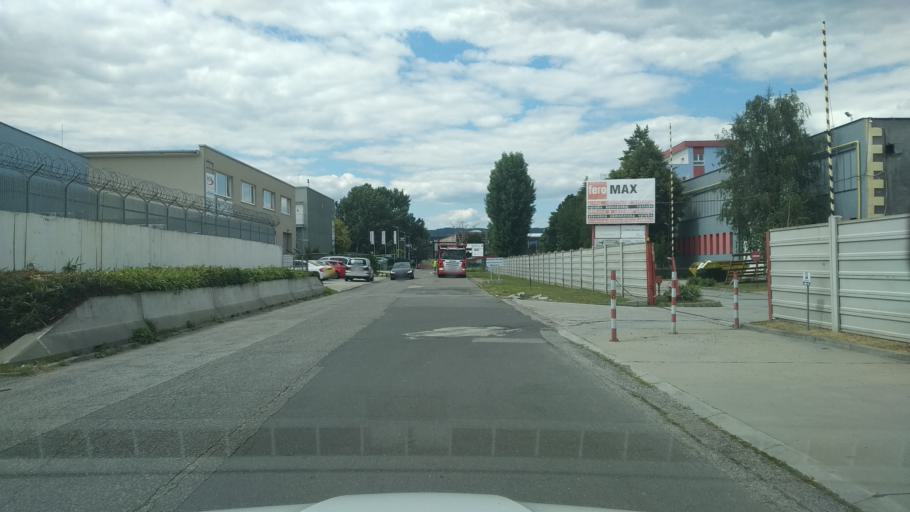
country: SK
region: Bratislavsky
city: Bratislava
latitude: 48.1821
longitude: 17.1682
